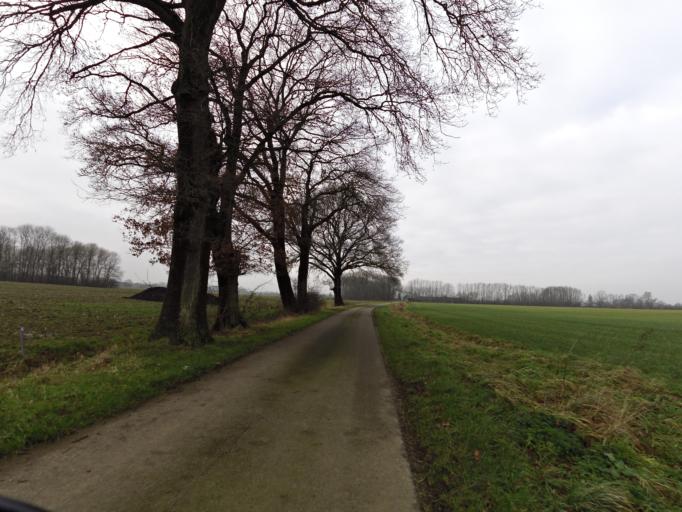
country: NL
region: Gelderland
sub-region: Gemeente Doesburg
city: Doesburg
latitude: 51.9947
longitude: 6.1777
